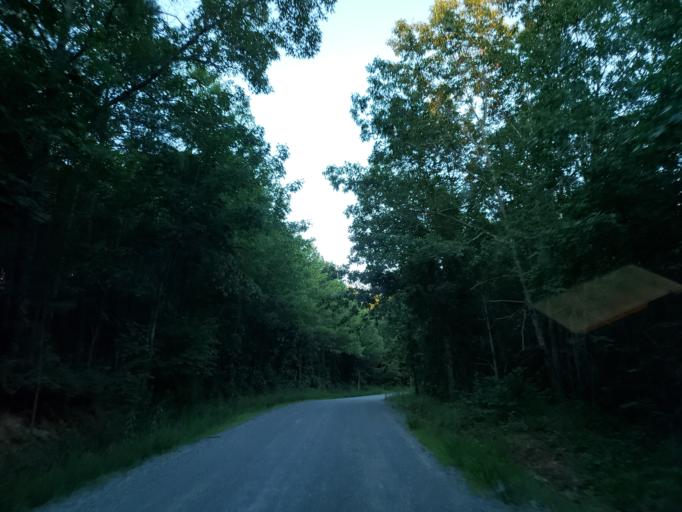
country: US
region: Georgia
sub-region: Bartow County
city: Euharlee
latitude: 34.0647
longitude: -84.8550
